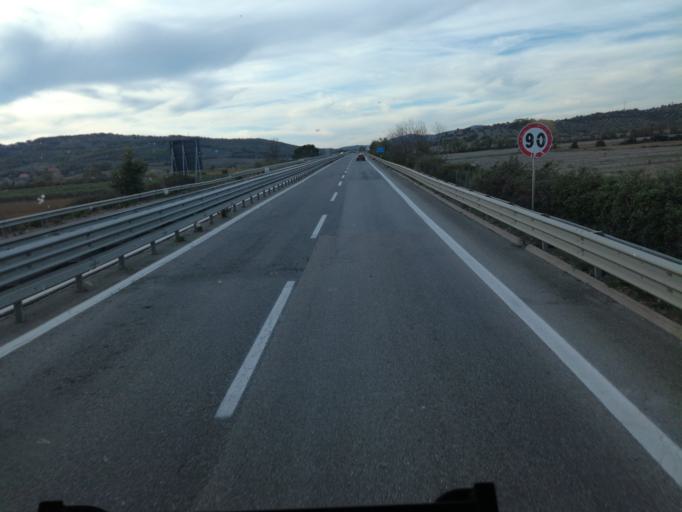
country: IT
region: Tuscany
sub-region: Provincia di Grosseto
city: Braccagni
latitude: 42.9082
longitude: 11.0275
